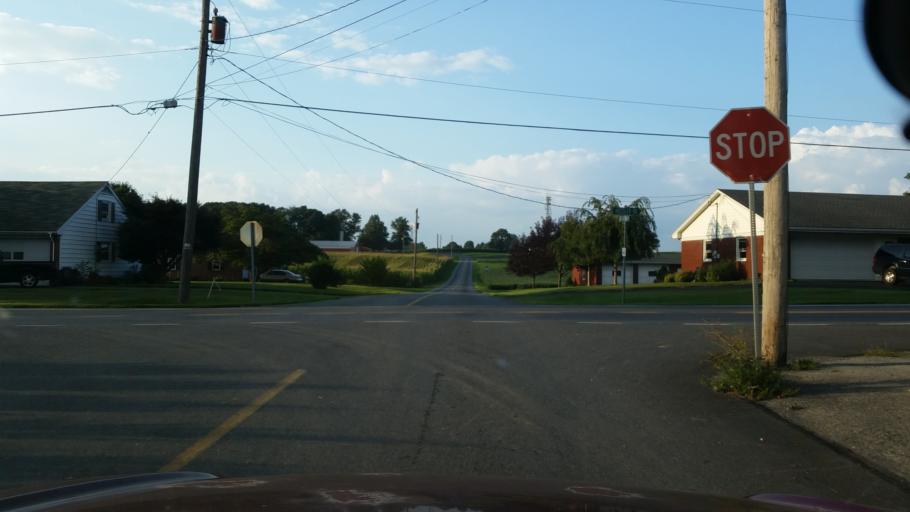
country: US
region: Pennsylvania
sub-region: Lancaster County
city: Manheim
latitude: 40.1637
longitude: -76.4558
